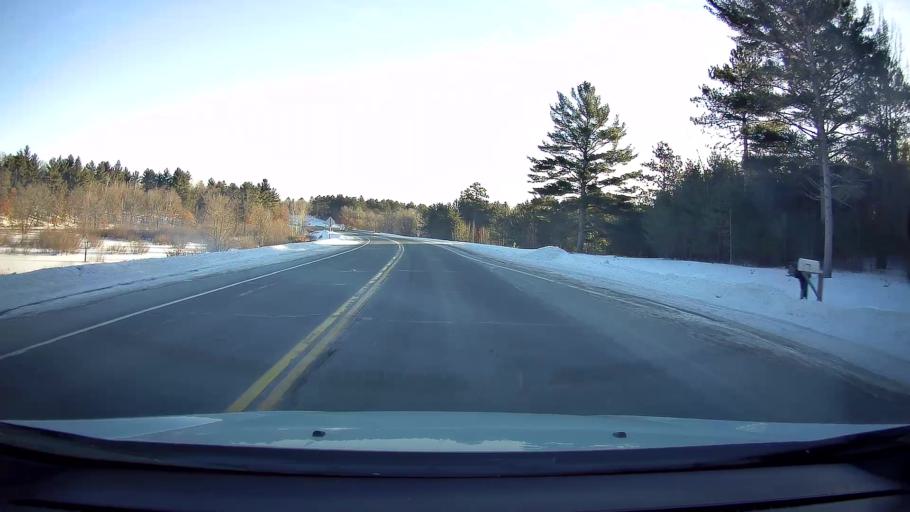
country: US
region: Wisconsin
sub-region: Washburn County
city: Spooner
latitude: 45.9051
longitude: -91.8153
